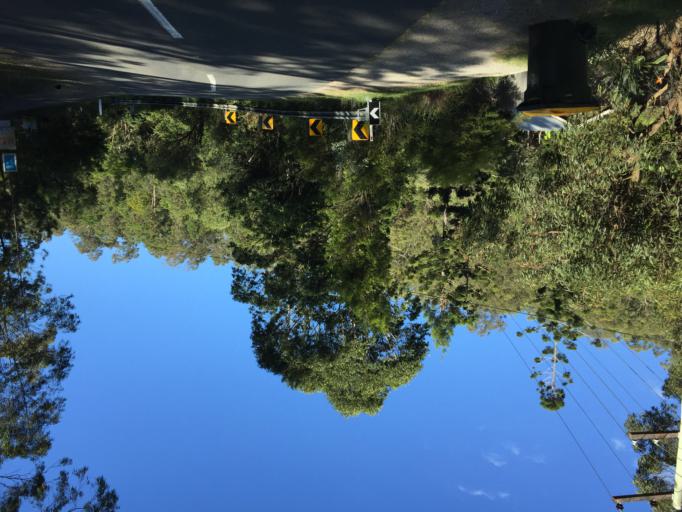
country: AU
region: Queensland
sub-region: Brisbane
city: Kenmore Hills
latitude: -27.4580
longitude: 152.9305
